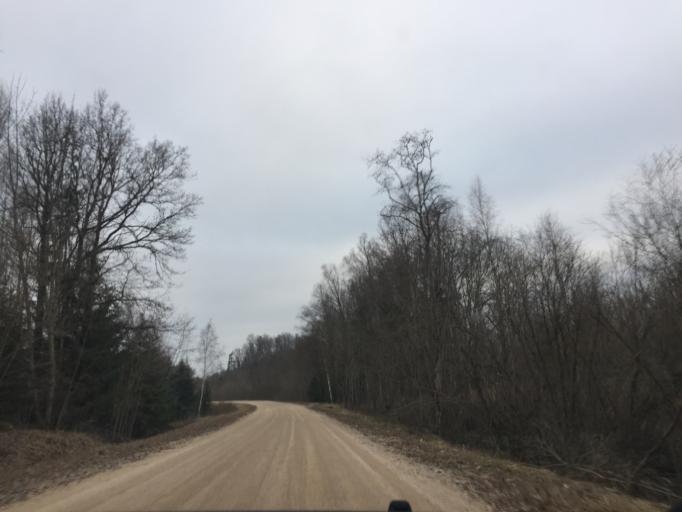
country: LV
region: Ligatne
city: Ligatne
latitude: 57.2190
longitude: 25.1269
